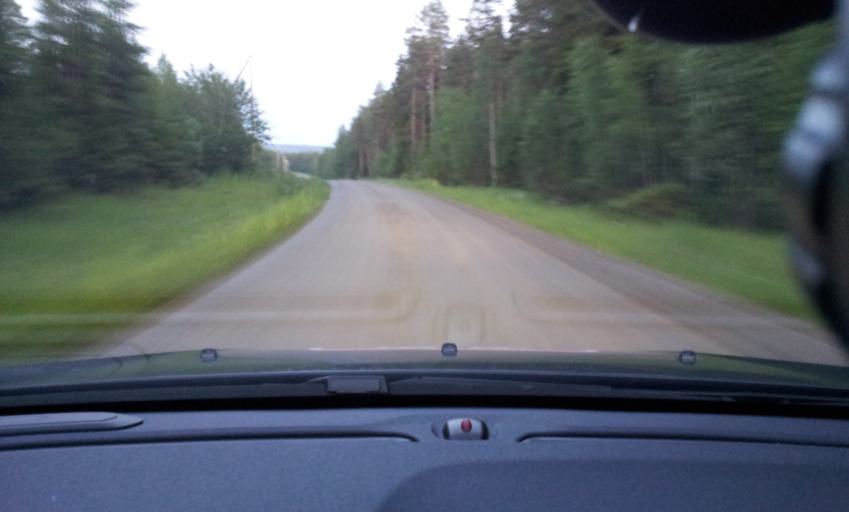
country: SE
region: Vaesternorrland
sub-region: Ange Kommun
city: Fransta
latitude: 62.8173
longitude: 16.0098
